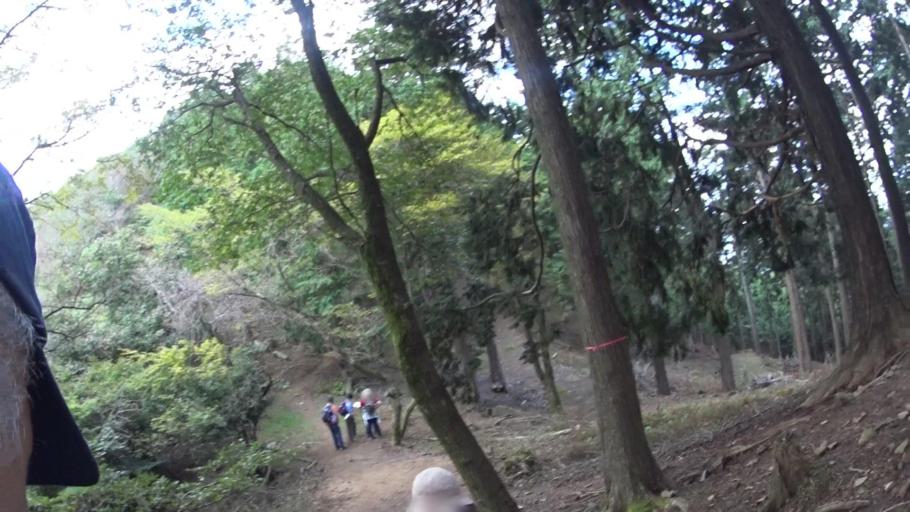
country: JP
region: Shiga Prefecture
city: Otsu-shi
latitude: 35.0940
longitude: 135.8373
